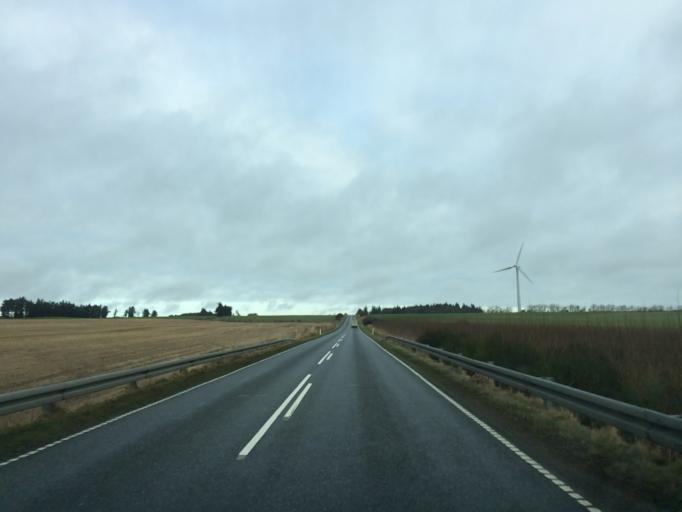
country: DK
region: Central Jutland
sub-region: Struer Kommune
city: Struer
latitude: 56.4215
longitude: 8.5015
